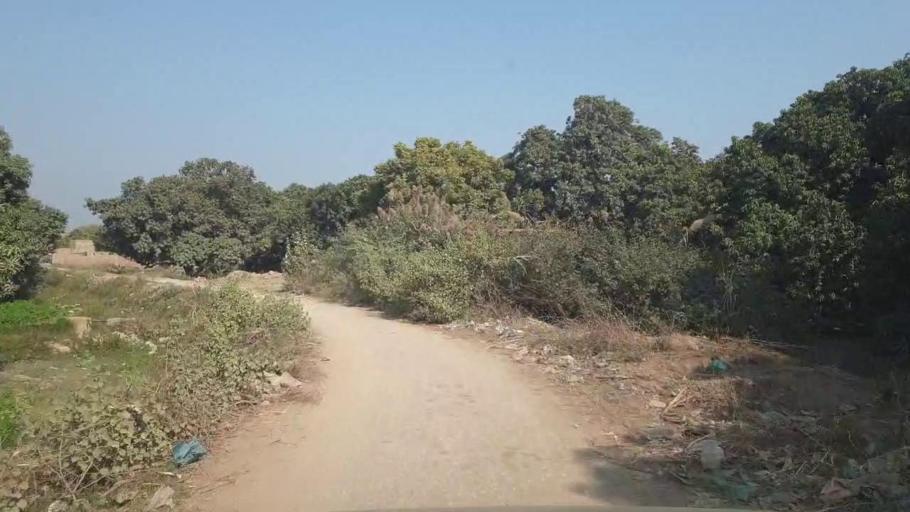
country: PK
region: Sindh
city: Tando Allahyar
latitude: 25.4739
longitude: 68.7839
